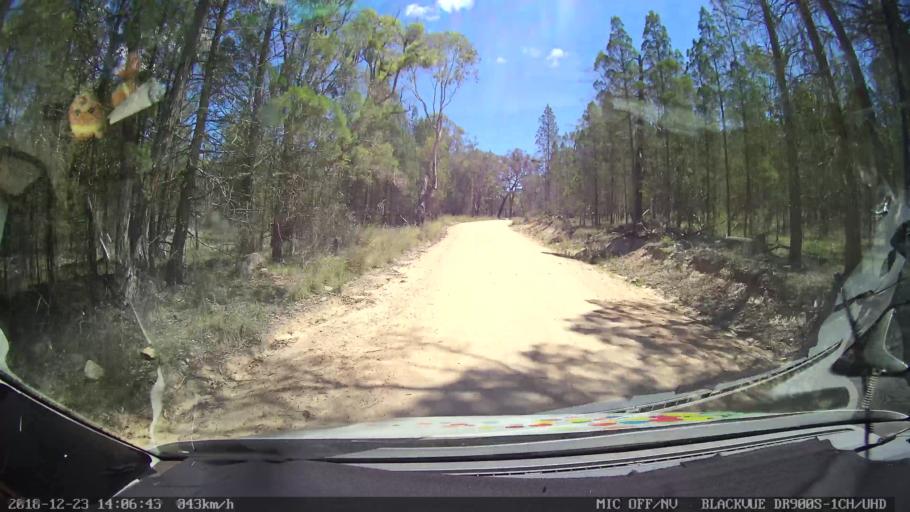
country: AU
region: New South Wales
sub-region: Tamworth Municipality
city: Manilla
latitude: -30.6316
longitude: 151.0746
